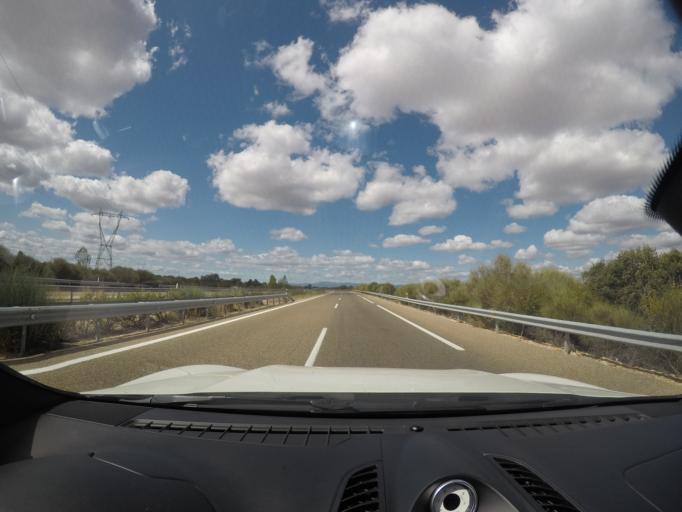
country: ES
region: Castille and Leon
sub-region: Provincia de Zamora
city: Calzadilla de Tera
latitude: 42.0054
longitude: -6.0680
